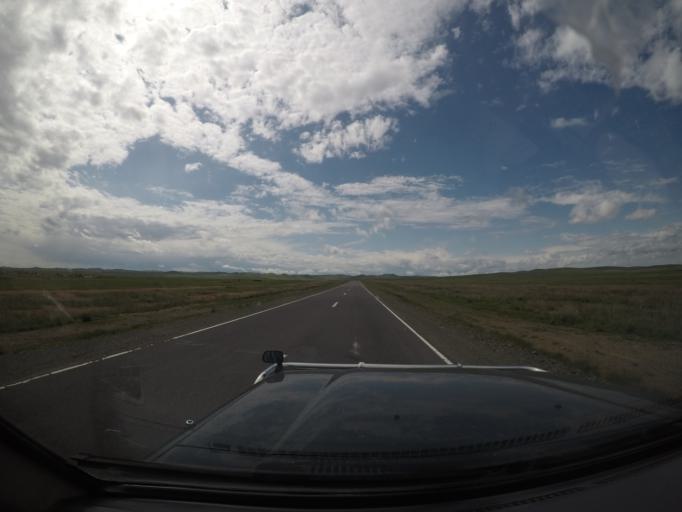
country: MN
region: Hentiy
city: Moron
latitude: 47.4185
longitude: 109.8995
